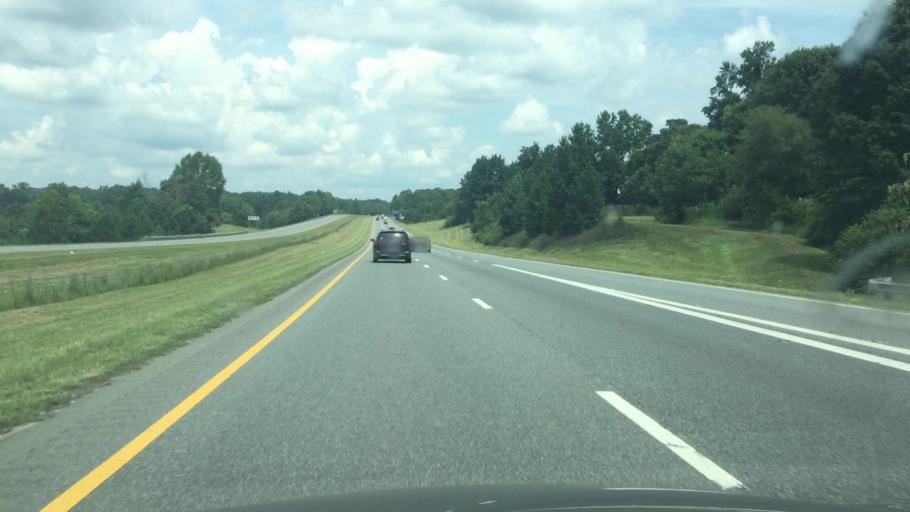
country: US
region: North Carolina
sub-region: Montgomery County
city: Biscoe
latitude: 35.4933
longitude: -79.7800
